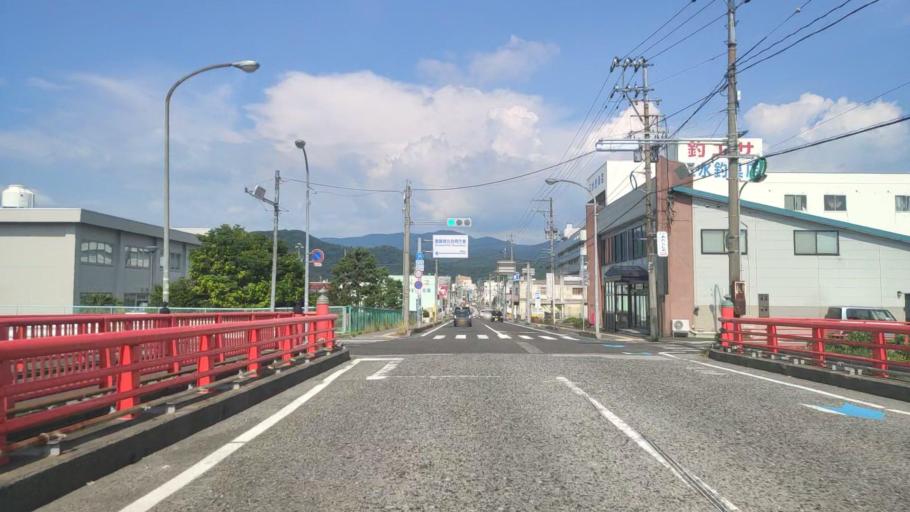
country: JP
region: Fukui
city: Tsuruga
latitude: 35.6528
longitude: 136.0616
